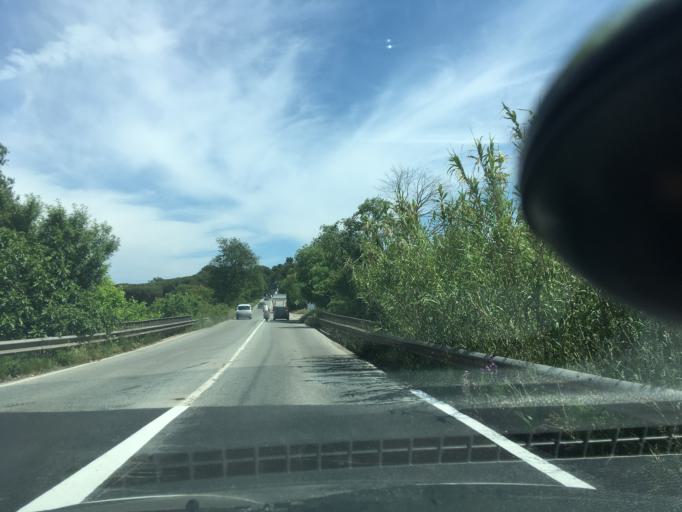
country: FR
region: Provence-Alpes-Cote d'Azur
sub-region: Departement du Var
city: Puget-sur-Argens
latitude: 43.4616
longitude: 6.6579
